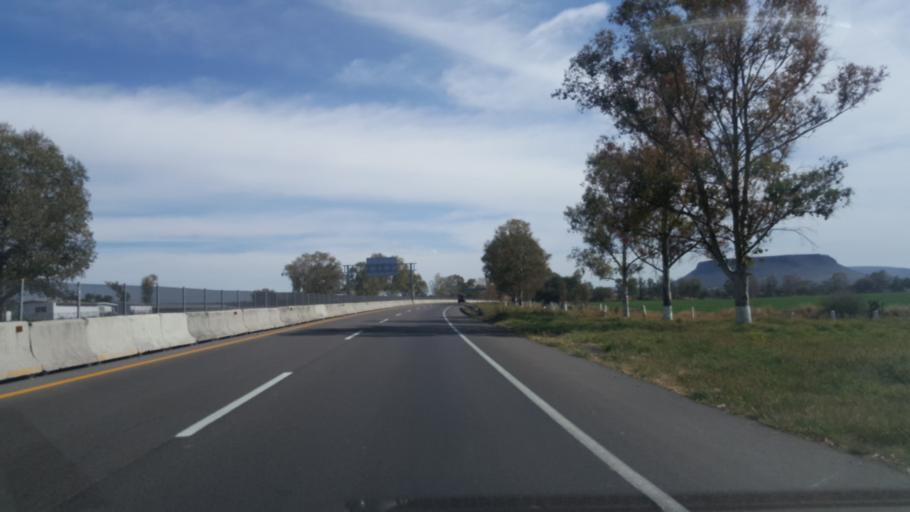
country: MX
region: Jalisco
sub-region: Lagos de Moreno
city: Cristeros [Fraccionamiento]
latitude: 21.3163
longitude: -102.0400
